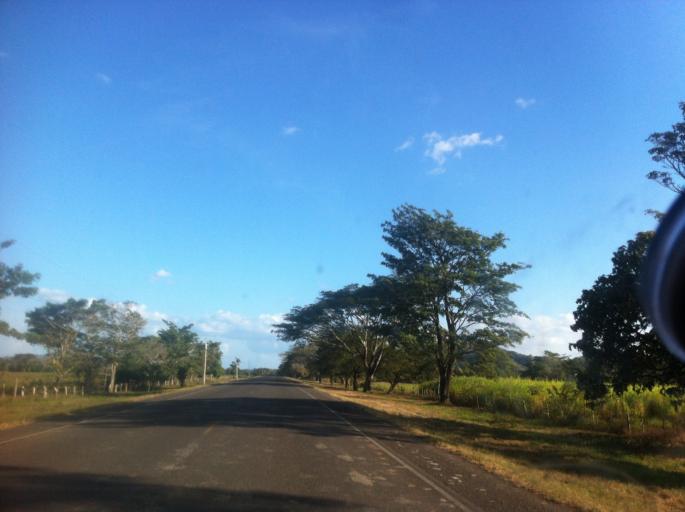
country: NI
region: Rio San Juan
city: Morrito
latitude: 11.7705
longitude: -85.0120
